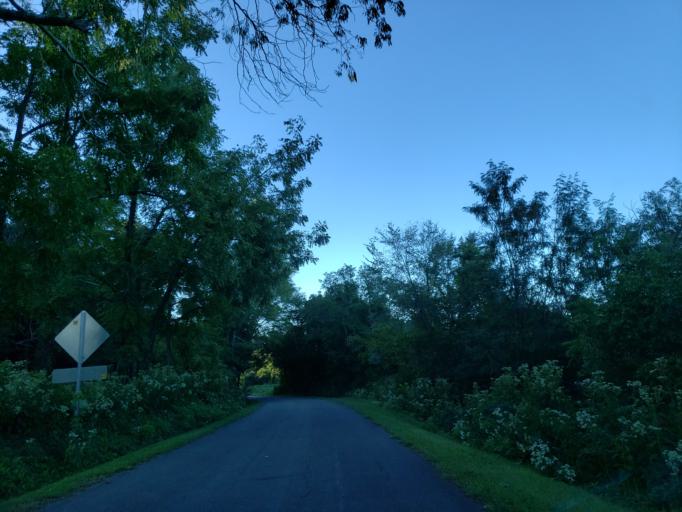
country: US
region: Georgia
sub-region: Bartow County
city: Rydal
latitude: 34.3358
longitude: -84.7164
